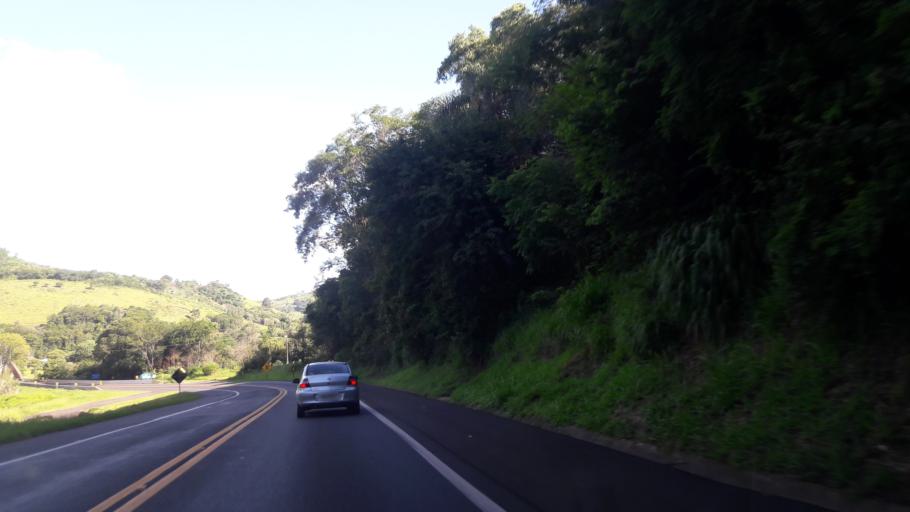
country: BR
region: Parana
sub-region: Laranjeiras Do Sul
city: Laranjeiras do Sul
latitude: -25.4179
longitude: -52.0698
